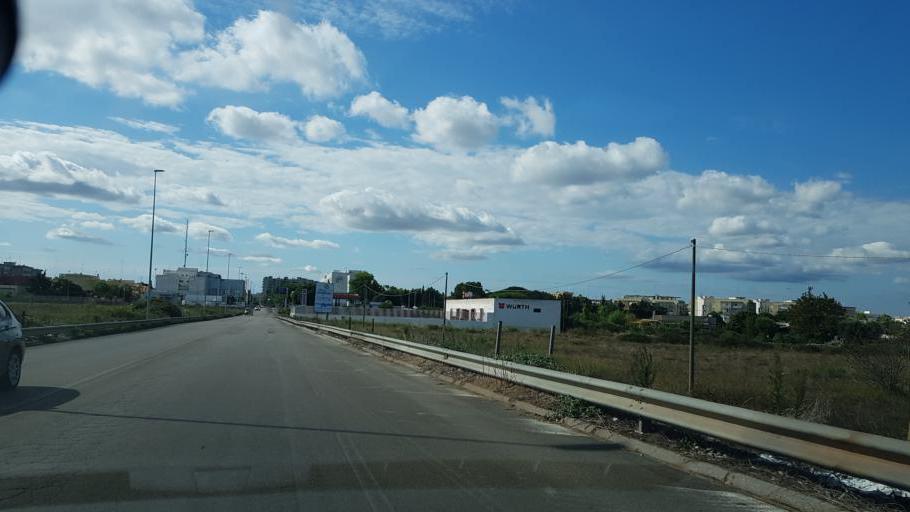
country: IT
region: Apulia
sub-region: Provincia di Lecce
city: Lecce
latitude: 40.3645
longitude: 18.1591
